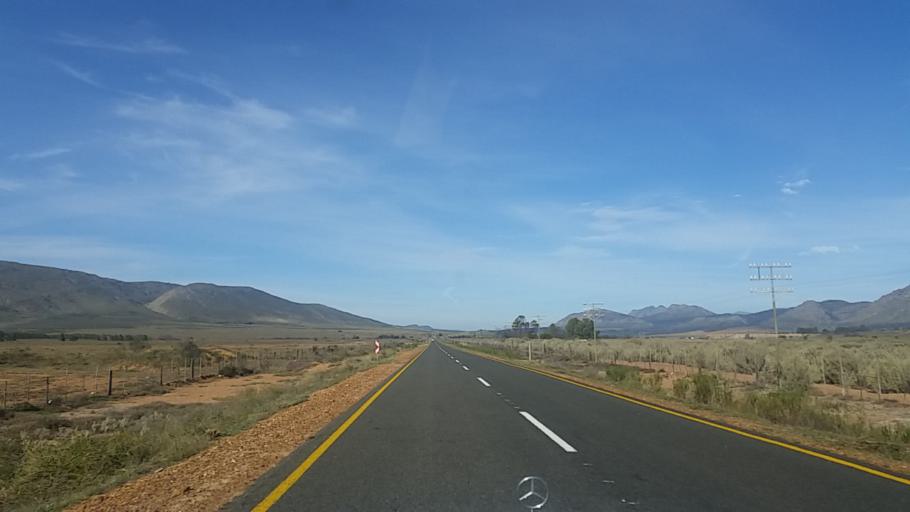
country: ZA
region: Western Cape
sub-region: Eden District Municipality
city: George
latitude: -33.8100
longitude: 22.5438
